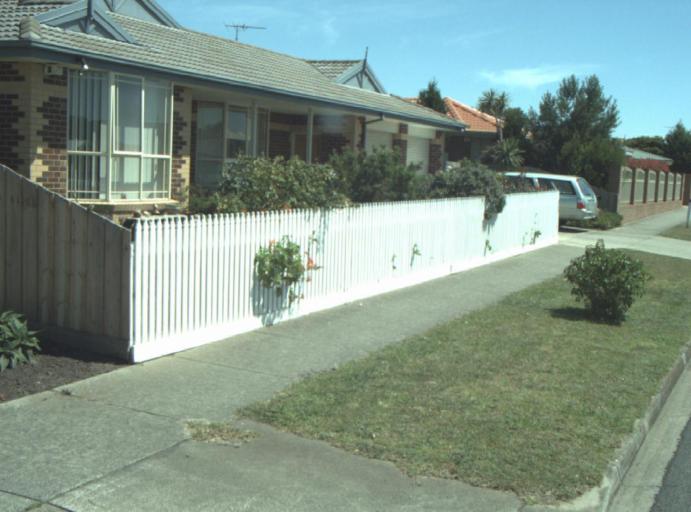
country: AU
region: Victoria
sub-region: Greater Geelong
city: Leopold
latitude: -38.1788
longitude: 144.4760
